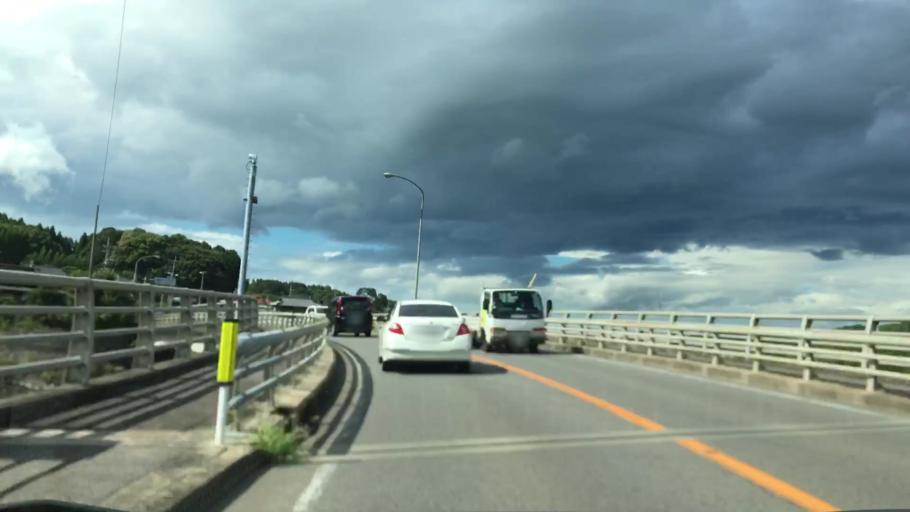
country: JP
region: Saga Prefecture
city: Imaricho-ko
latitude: 33.2407
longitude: 129.8508
